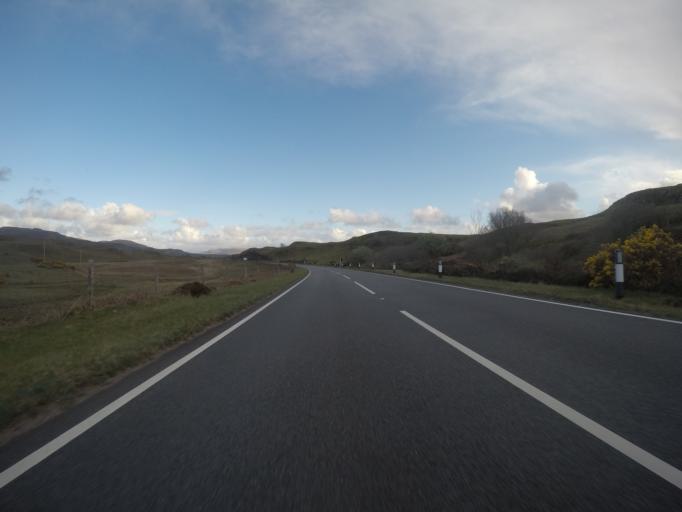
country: GB
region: Scotland
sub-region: Highland
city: Isle of Skye
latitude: 57.5115
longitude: -6.3404
